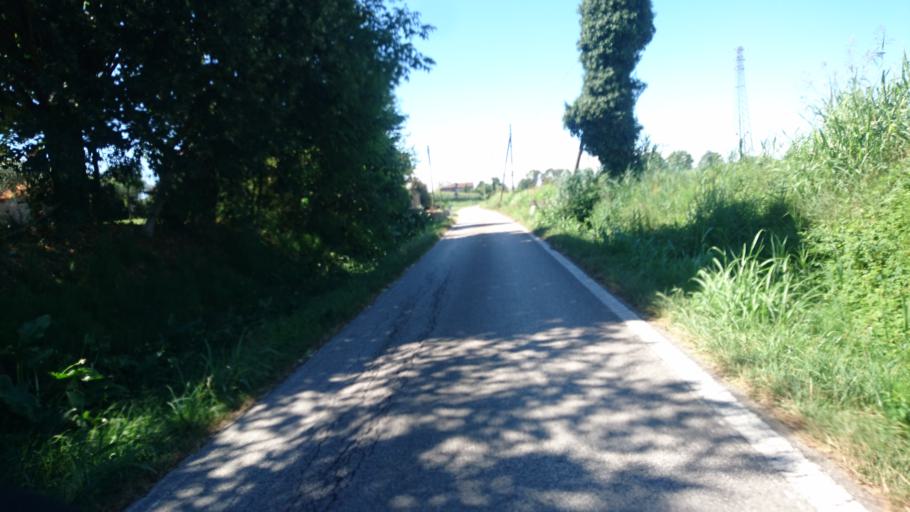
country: IT
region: Veneto
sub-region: Provincia di Padova
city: Campagnola
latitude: 45.2732
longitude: 12.0191
